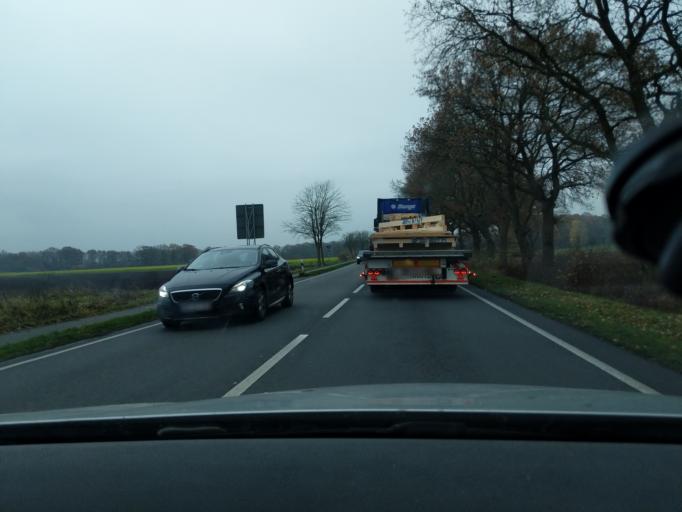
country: DE
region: Lower Saxony
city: Zeven
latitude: 53.2742
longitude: 9.2757
